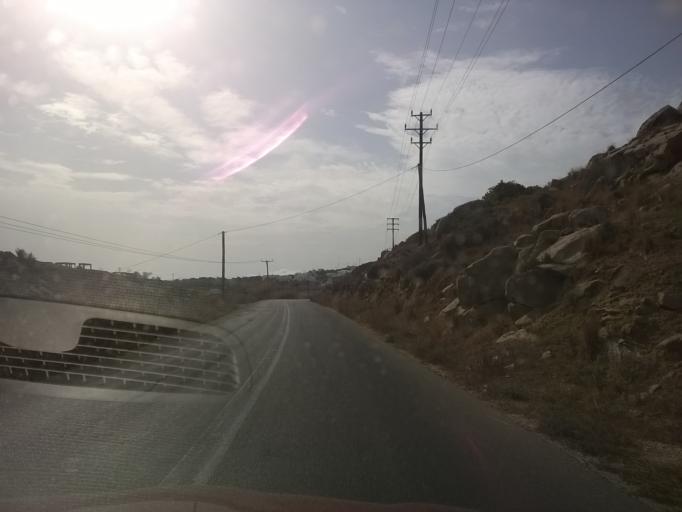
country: GR
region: South Aegean
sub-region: Nomos Kykladon
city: Naxos
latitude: 37.0867
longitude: 25.3553
